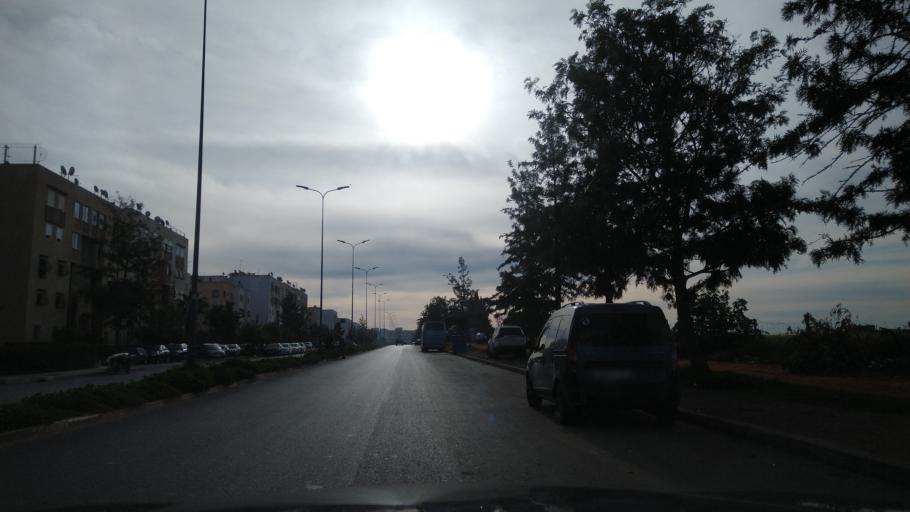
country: MA
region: Rabat-Sale-Zemmour-Zaer
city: Sale
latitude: 33.9926
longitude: -6.7433
